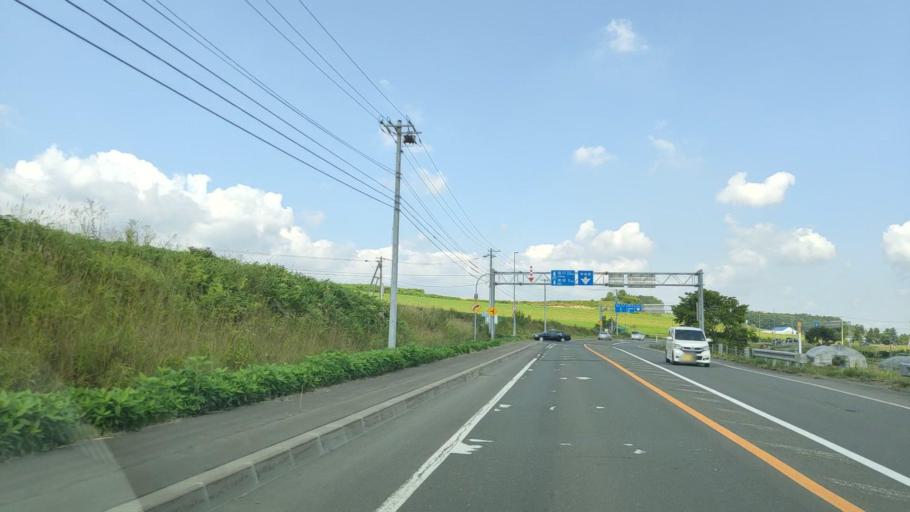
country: JP
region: Hokkaido
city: Shimo-furano
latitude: 43.5321
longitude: 142.4420
